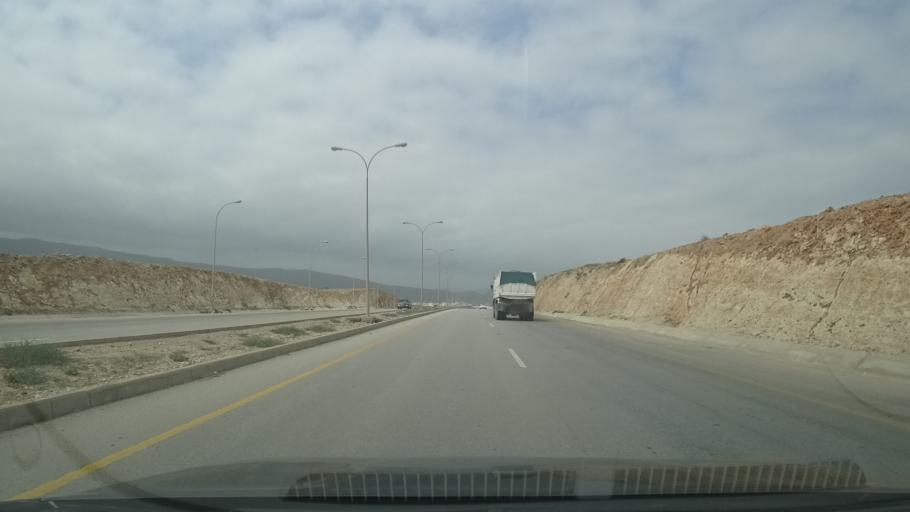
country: OM
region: Zufar
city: Salalah
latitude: 17.0456
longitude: 54.3807
